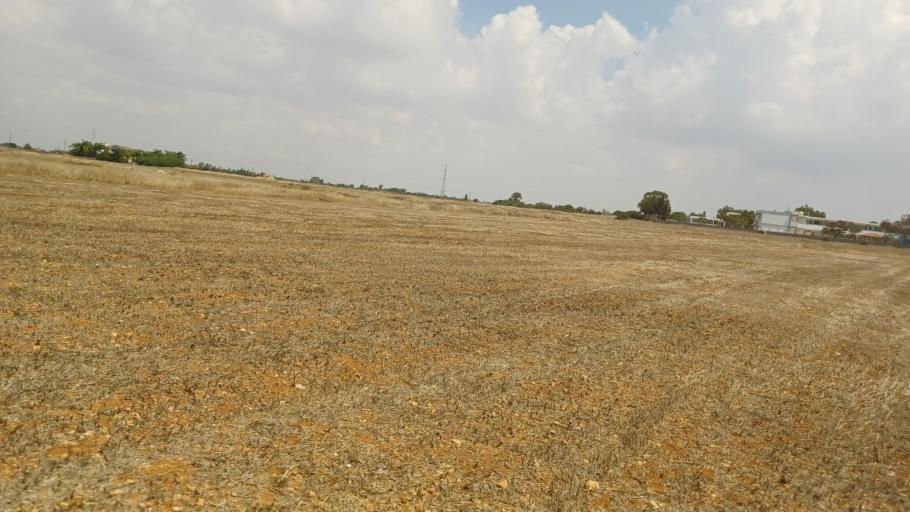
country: CY
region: Ammochostos
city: Liopetri
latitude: 34.9906
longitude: 33.8613
